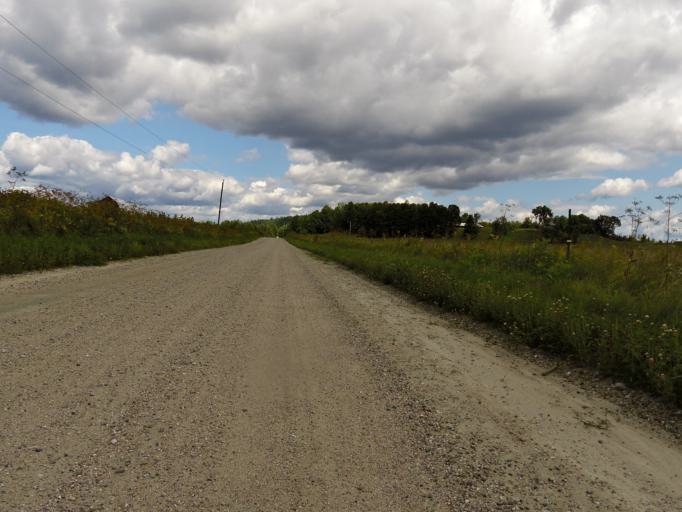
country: CA
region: Quebec
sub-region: Outaouais
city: Wakefield
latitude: 45.7885
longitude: -76.0275
